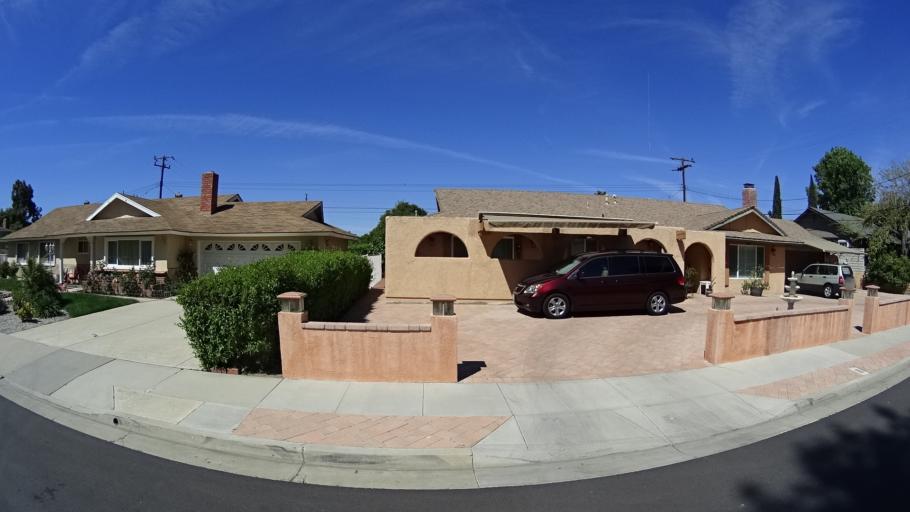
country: US
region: California
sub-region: Ventura County
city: Moorpark
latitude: 34.2265
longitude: -118.8668
